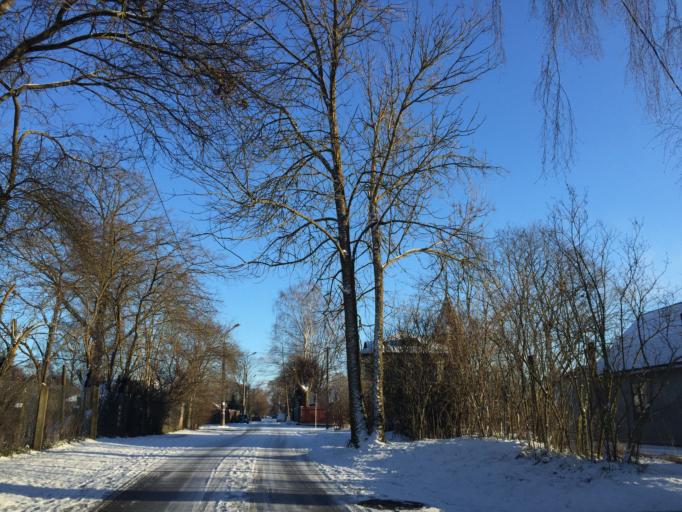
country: LV
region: Marupe
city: Marupe
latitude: 56.9113
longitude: 24.0576
